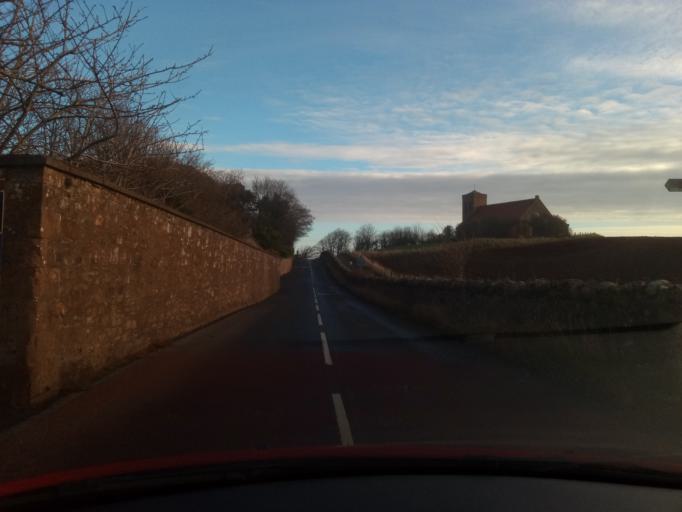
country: GB
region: Scotland
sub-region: The Scottish Borders
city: Eyemouth
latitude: 55.9001
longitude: -2.1359
